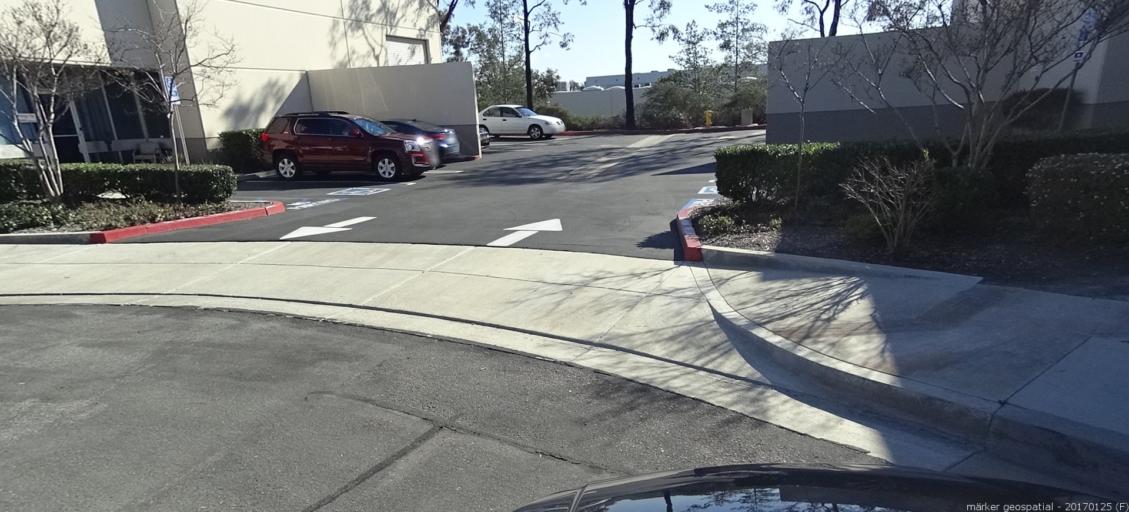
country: US
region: California
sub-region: Orange County
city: Lake Forest
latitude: 33.6656
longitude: -117.6778
